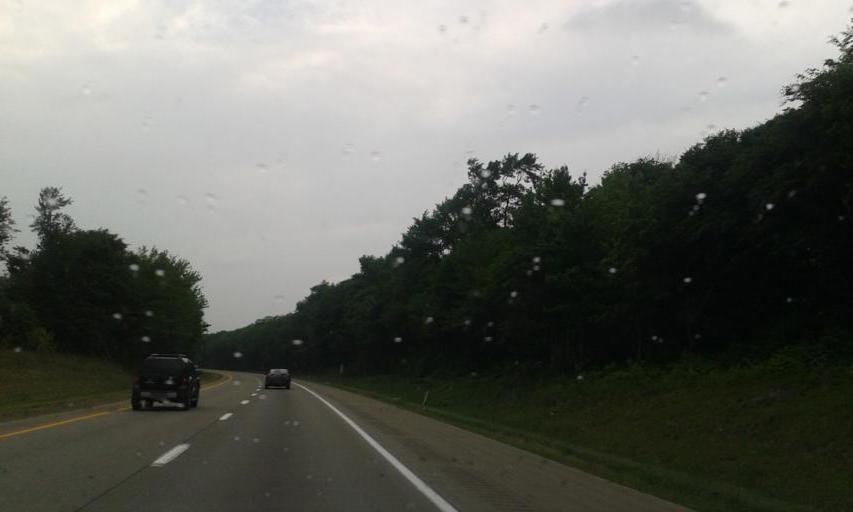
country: US
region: Pennsylvania
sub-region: Monroe County
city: Mount Pocono
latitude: 41.1434
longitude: -75.4026
